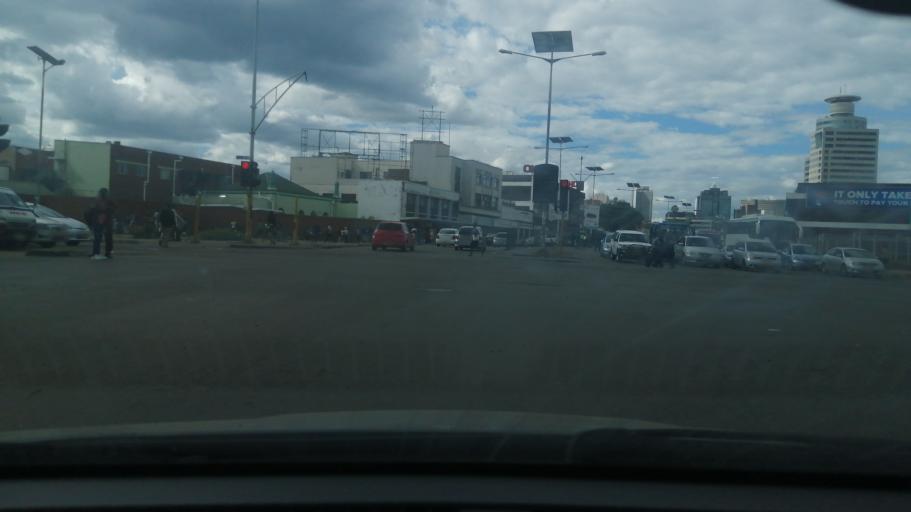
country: ZW
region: Harare
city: Harare
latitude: -17.8363
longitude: 31.0468
